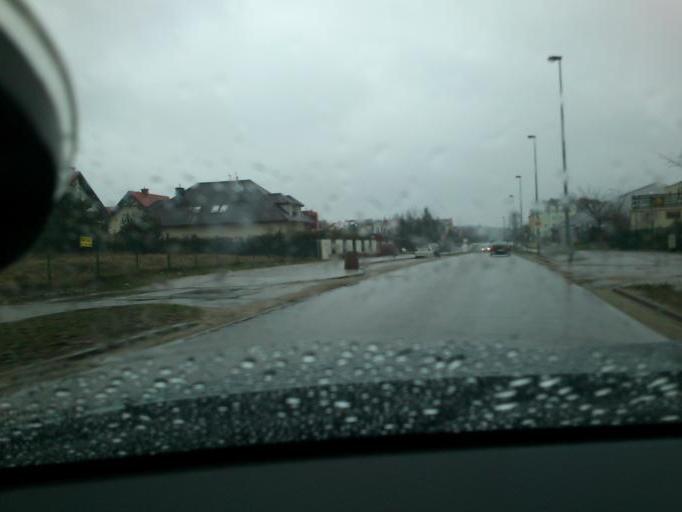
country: PL
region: Pomeranian Voivodeship
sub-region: Gdynia
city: Wielki Kack
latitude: 54.4249
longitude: 18.4747
